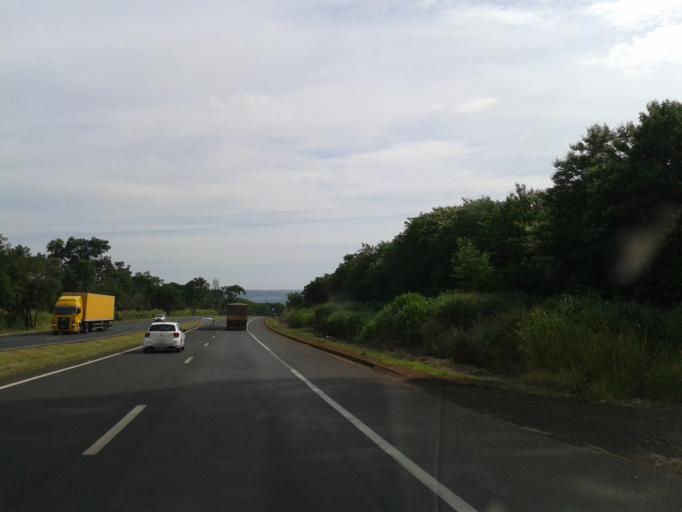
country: BR
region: Minas Gerais
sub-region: Uberlandia
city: Uberlandia
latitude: -18.8128
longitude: -48.2481
